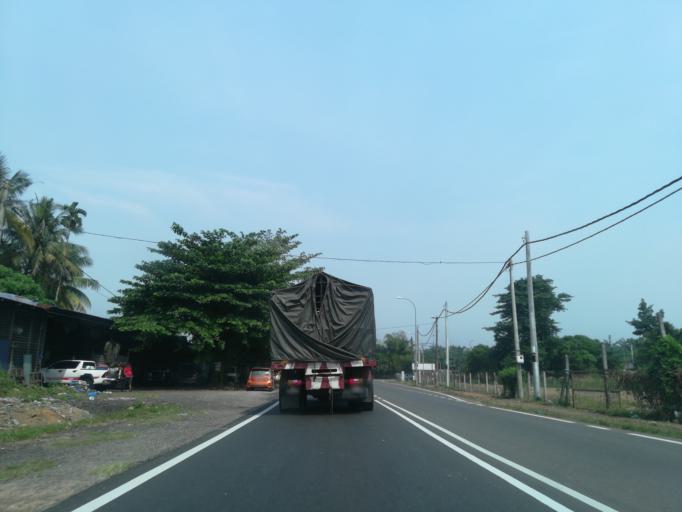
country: MY
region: Penang
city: Tasek Glugor
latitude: 5.4635
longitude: 100.5442
